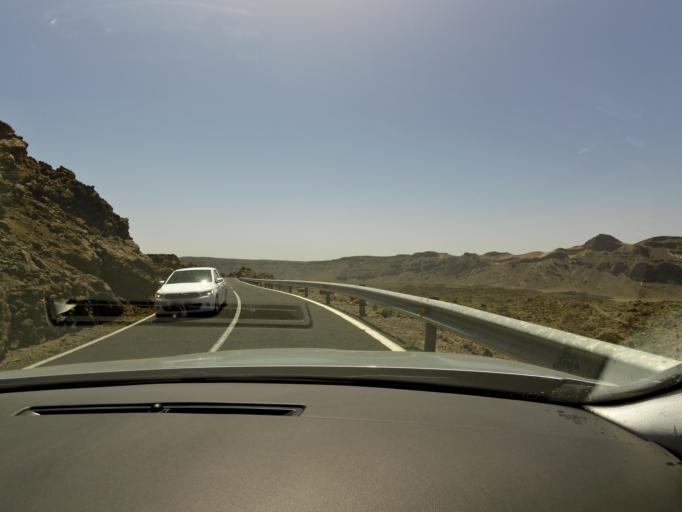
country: ES
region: Canary Islands
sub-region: Provincia de Santa Cruz de Tenerife
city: Los Realejos
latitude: 28.2607
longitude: -16.5953
